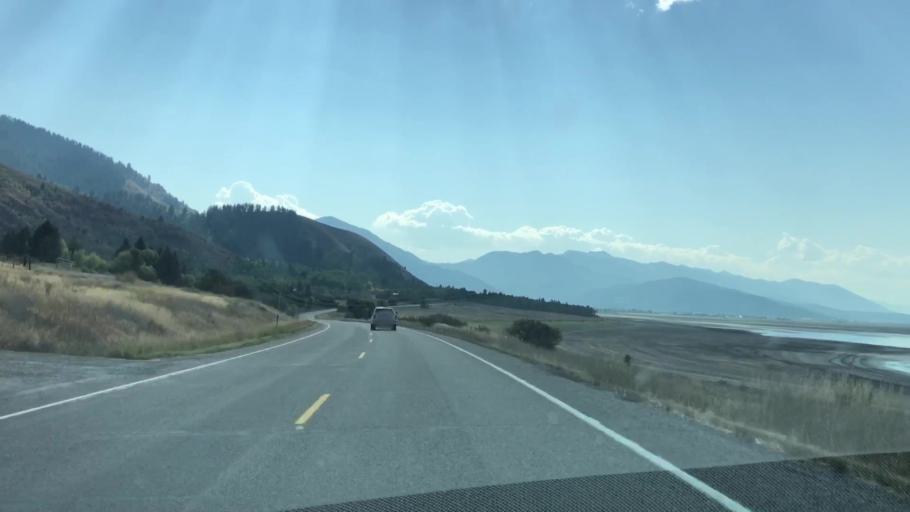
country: US
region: Wyoming
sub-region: Teton County
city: Hoback
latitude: 43.2192
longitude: -111.0706
